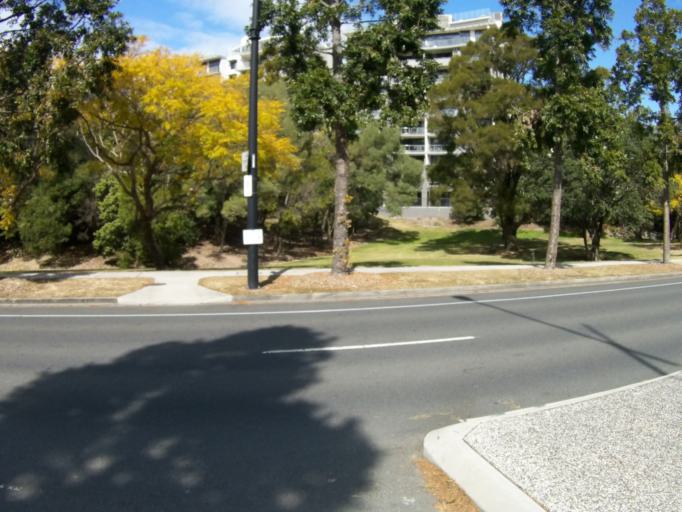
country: AU
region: Queensland
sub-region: Brisbane
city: Toowong
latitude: -27.4795
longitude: 152.9976
